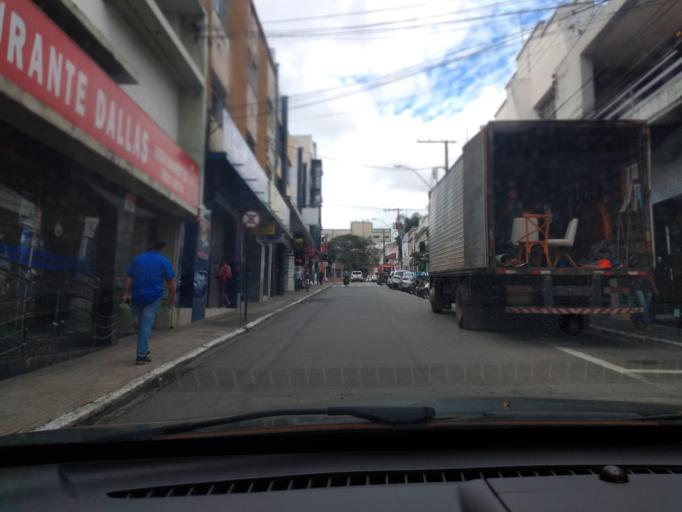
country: BR
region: Minas Gerais
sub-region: Lavras
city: Lavras
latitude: -21.2390
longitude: -44.9987
